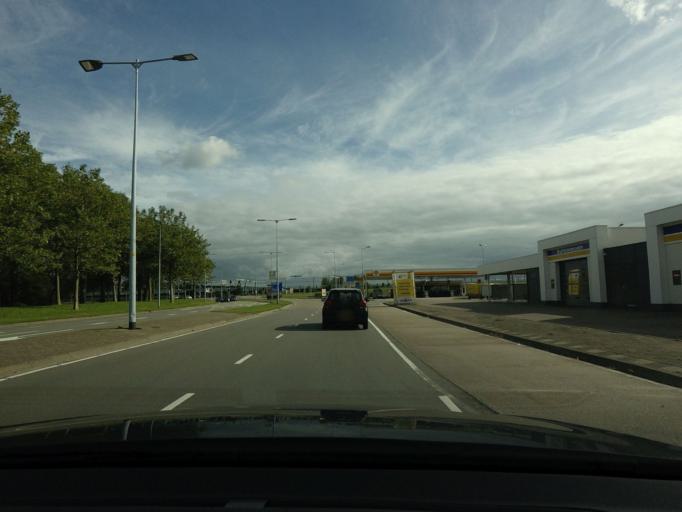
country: NL
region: North Holland
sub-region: Gemeente Haarlemmermeer
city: Hoofddorp
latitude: 52.2918
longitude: 4.6904
